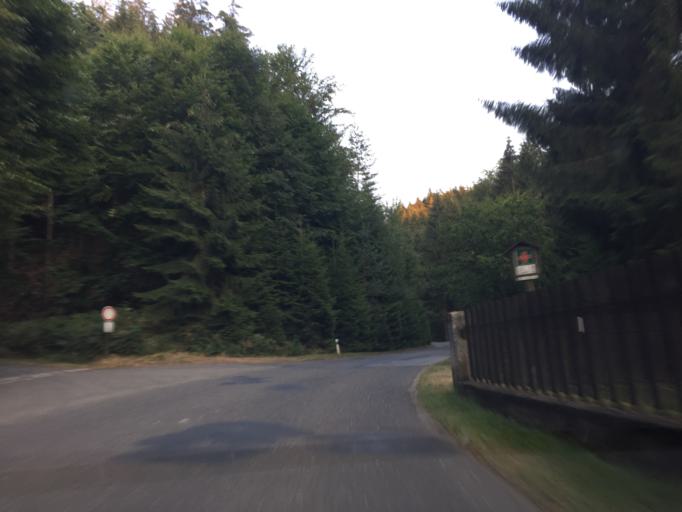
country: DE
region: Saxony
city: Sebnitz
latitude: 50.8801
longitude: 14.2756
